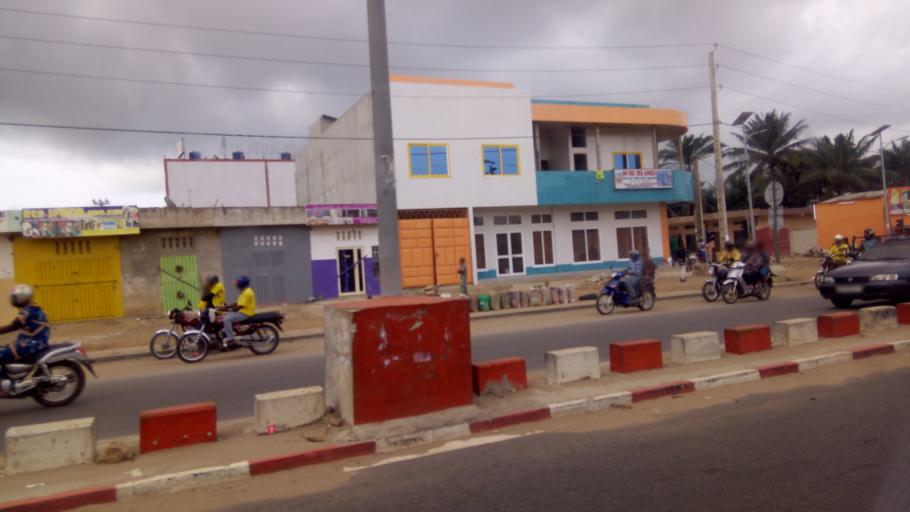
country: BJ
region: Atlantique
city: Hevie
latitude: 6.3890
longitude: 2.3132
